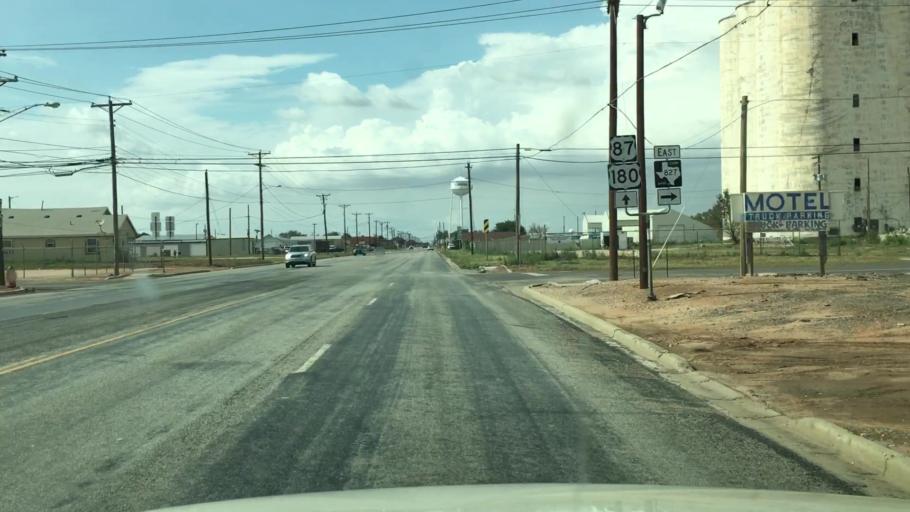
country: US
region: Texas
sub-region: Dawson County
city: Lamesa
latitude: 32.7259
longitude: -101.9469
